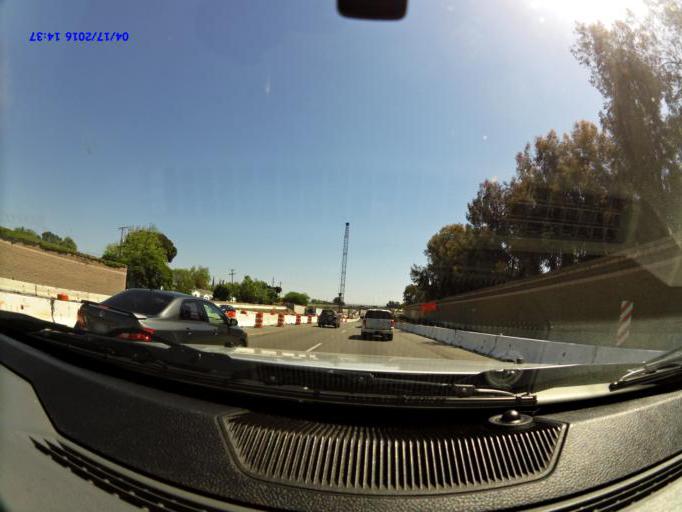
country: US
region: California
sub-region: San Joaquin County
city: Garden Acres
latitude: 37.9557
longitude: -121.2399
